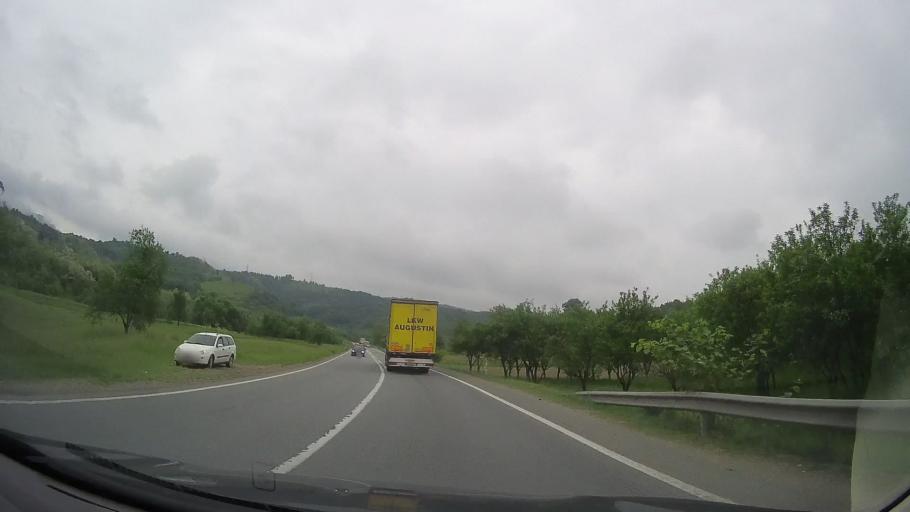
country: RO
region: Caras-Severin
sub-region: Comuna Teregova
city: Teregova
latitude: 45.1428
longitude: 22.3090
